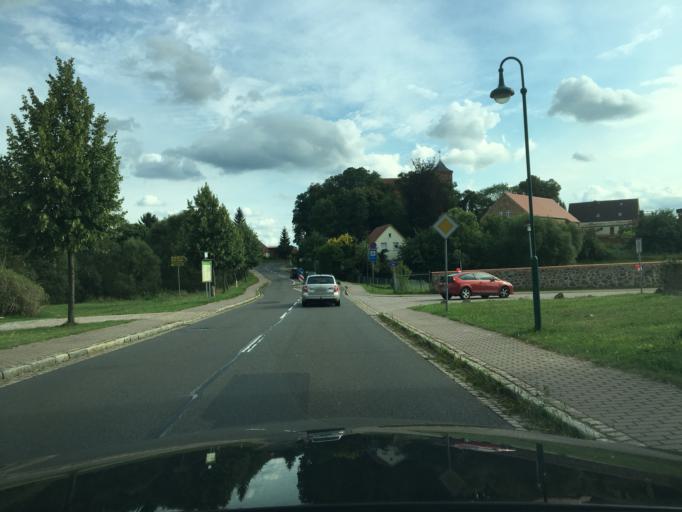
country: DE
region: Mecklenburg-Vorpommern
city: Penzlin
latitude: 53.4485
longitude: 13.0526
